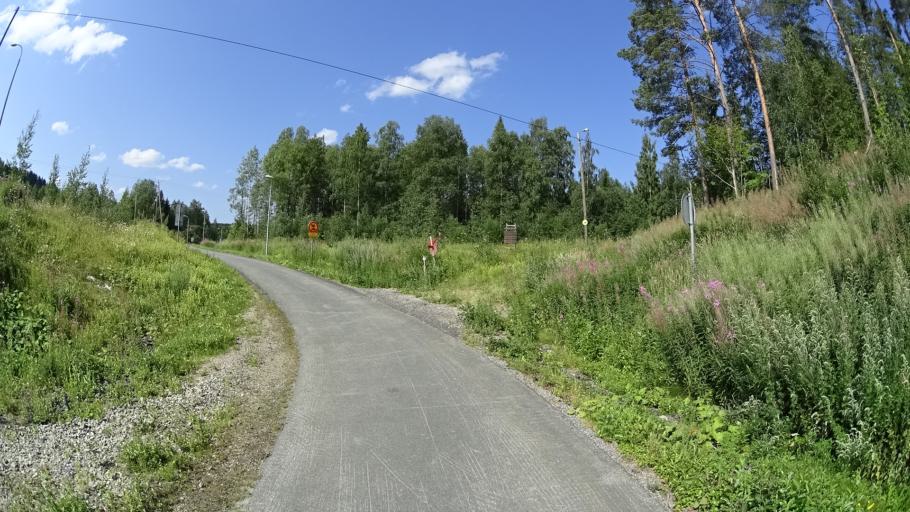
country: FI
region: North Karelia
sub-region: Pielisen Karjala
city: Lieksa
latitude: 63.1196
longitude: 29.8036
